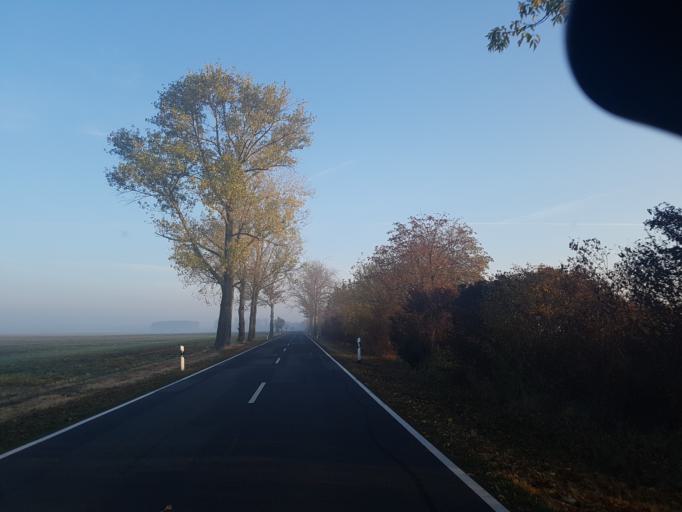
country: DE
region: Brandenburg
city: Juterbog
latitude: 51.9199
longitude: 13.0867
